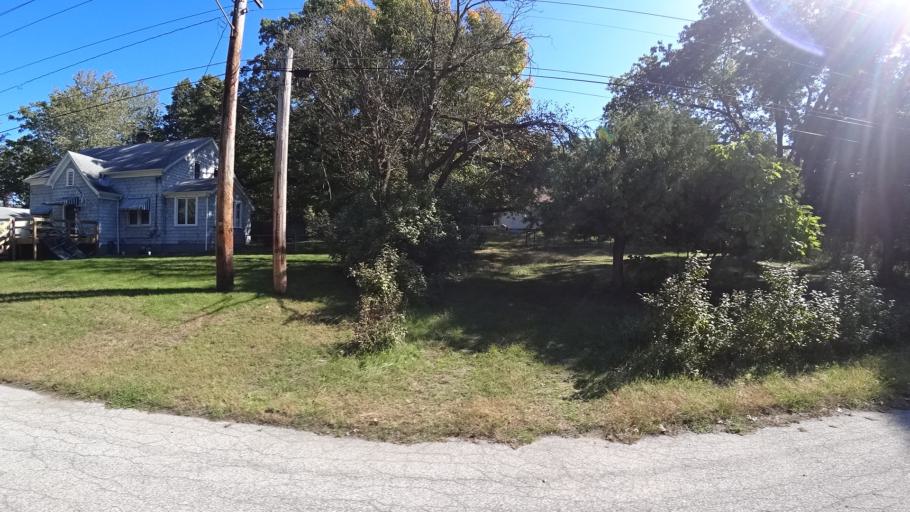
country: US
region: Indiana
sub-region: LaPorte County
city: Michigan City
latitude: 41.6996
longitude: -86.9218
